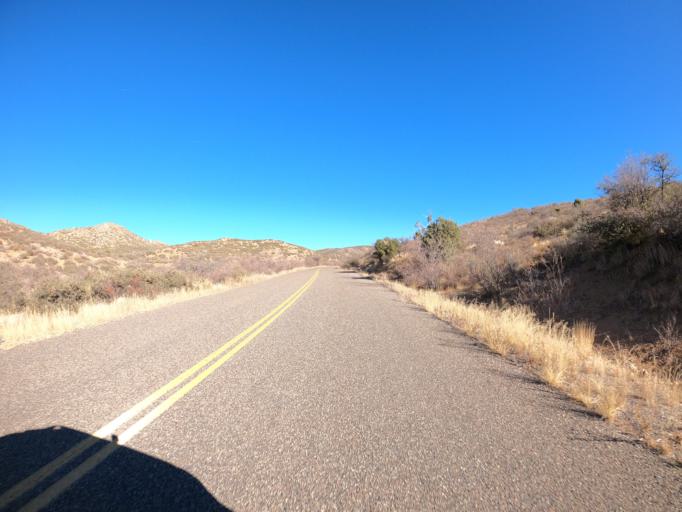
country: US
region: Arizona
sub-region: Yavapai County
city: Dewey-Humboldt
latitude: 34.5486
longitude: -112.0757
